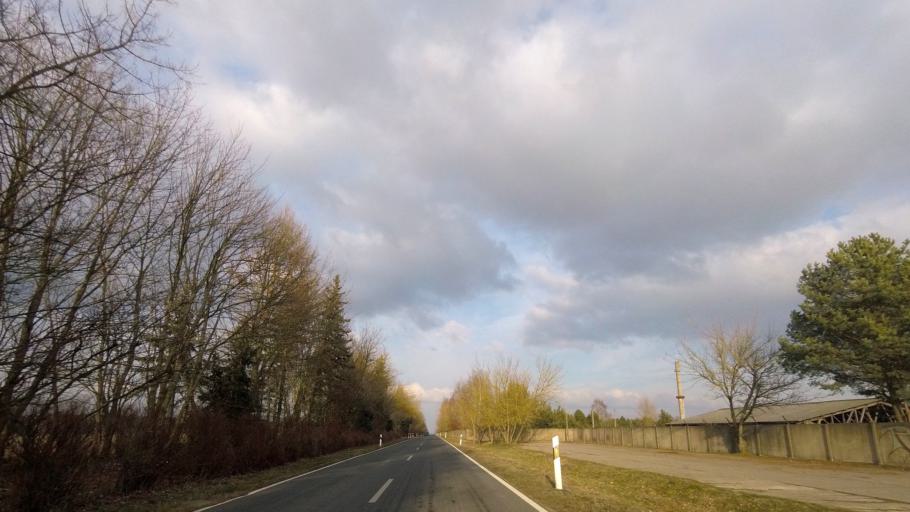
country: DE
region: Brandenburg
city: Belzig
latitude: 52.1162
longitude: 12.5770
